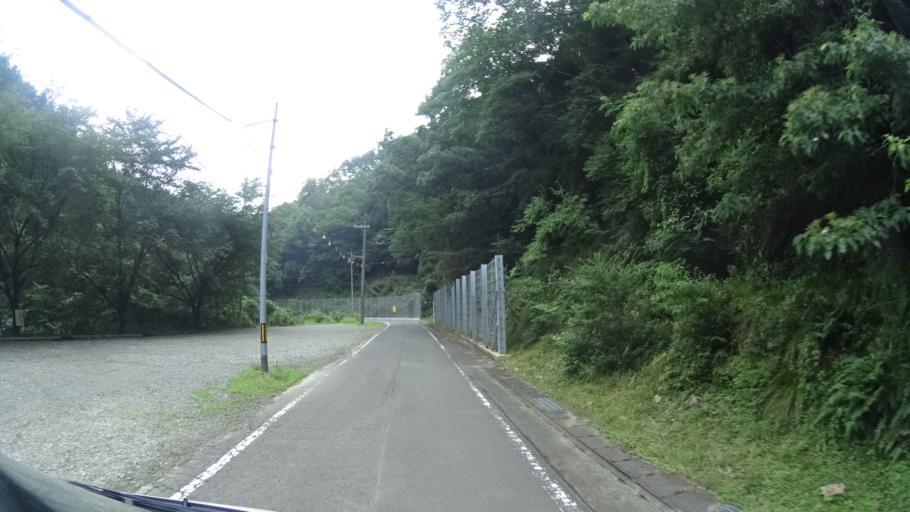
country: JP
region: Hyogo
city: Sasayama
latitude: 35.1814
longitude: 135.2173
